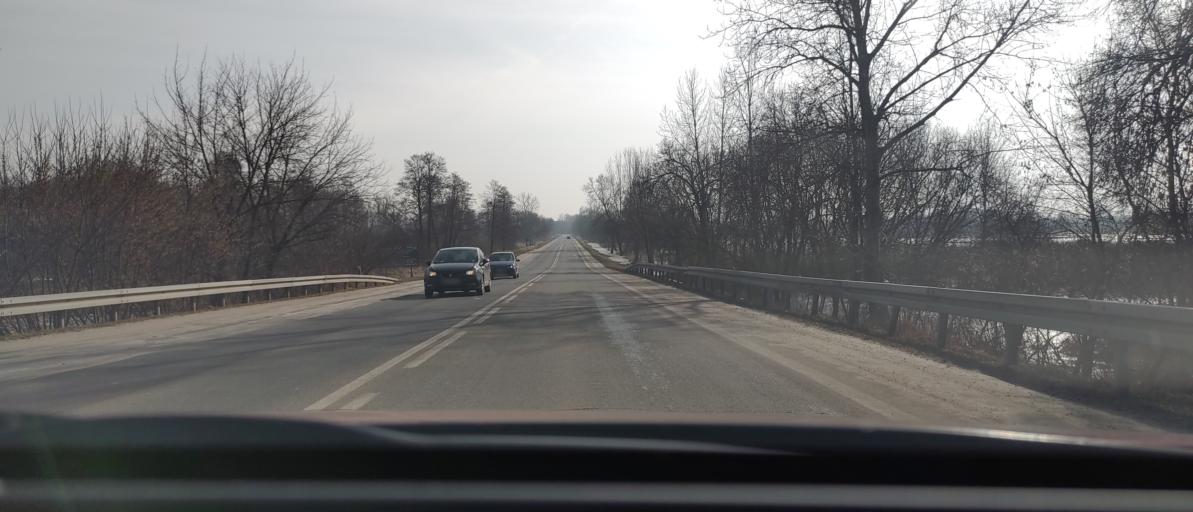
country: PL
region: Masovian Voivodeship
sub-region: Powiat bialobrzeski
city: Promna
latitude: 51.6705
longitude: 20.9450
